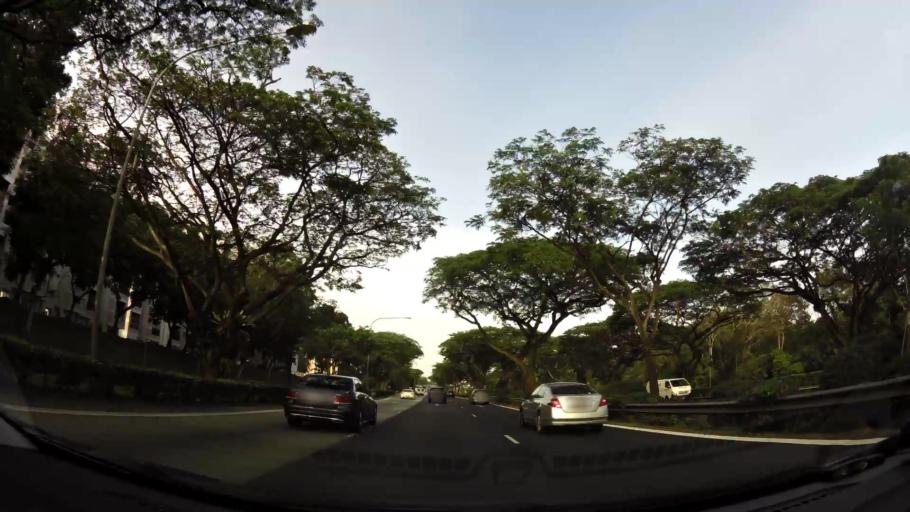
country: MY
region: Johor
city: Johor Bahru
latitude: 1.3554
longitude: 103.7225
